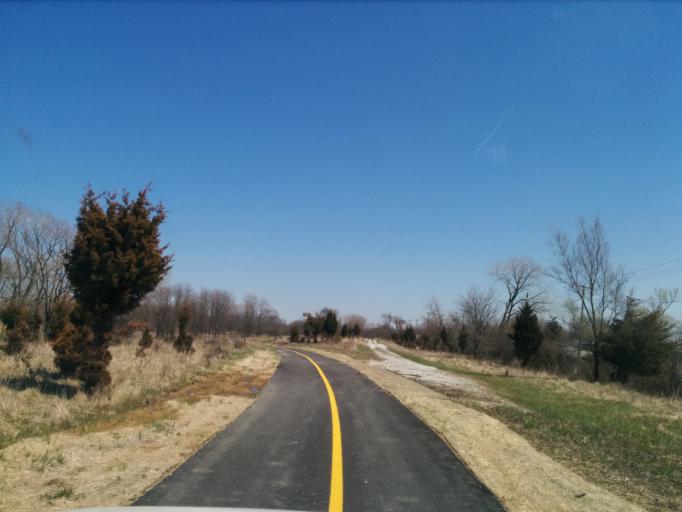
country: US
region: Illinois
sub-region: Cook County
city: Oak Forest
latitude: 41.5963
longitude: -87.7273
